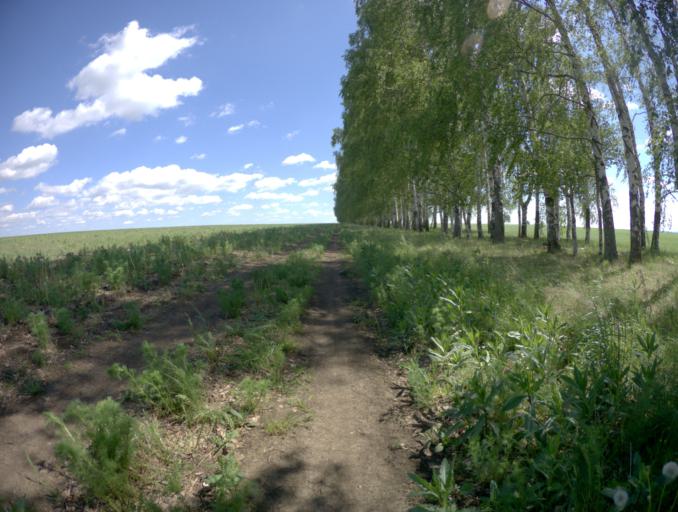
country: RU
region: Ivanovo
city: Gavrilov Posad
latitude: 56.4527
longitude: 40.2218
